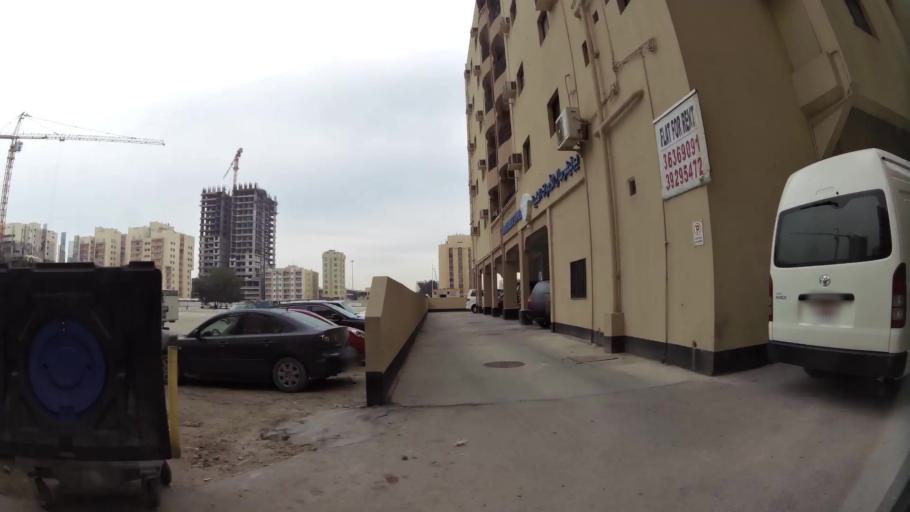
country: BH
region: Manama
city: Manama
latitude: 26.2367
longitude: 50.5929
